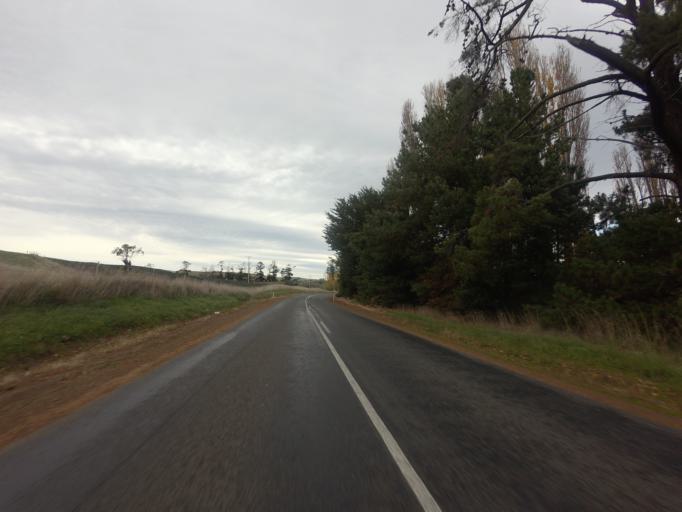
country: AU
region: Tasmania
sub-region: Derwent Valley
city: New Norfolk
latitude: -42.5177
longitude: 146.7476
